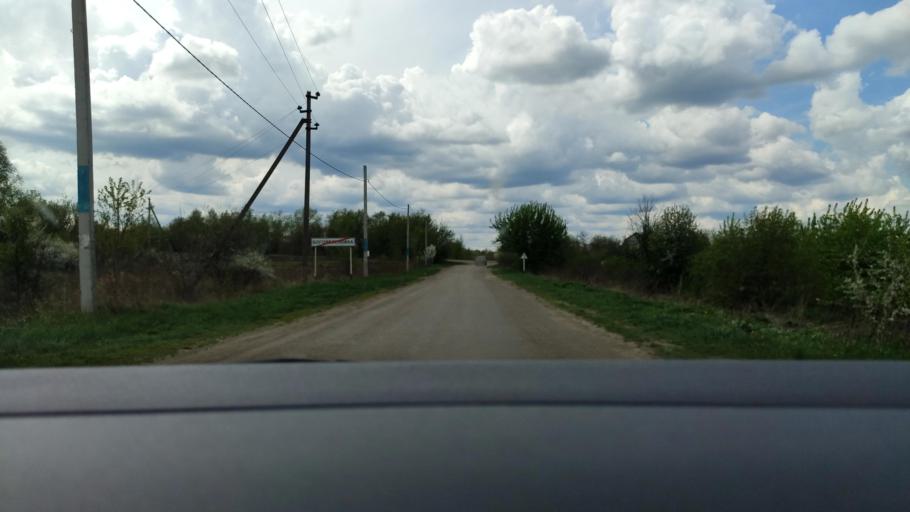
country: RU
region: Voronezj
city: Semiluki
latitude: 51.7785
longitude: 38.9974
